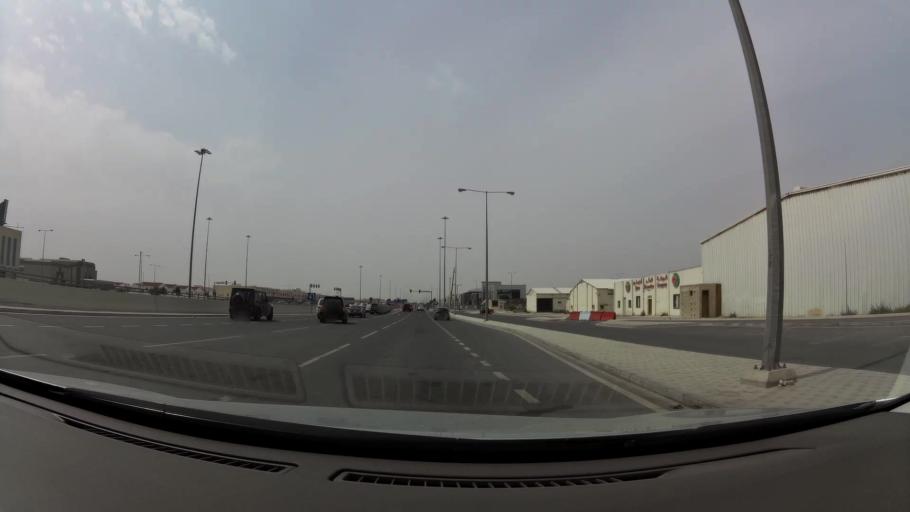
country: QA
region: Baladiyat ad Dawhah
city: Doha
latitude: 25.2578
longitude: 51.4859
